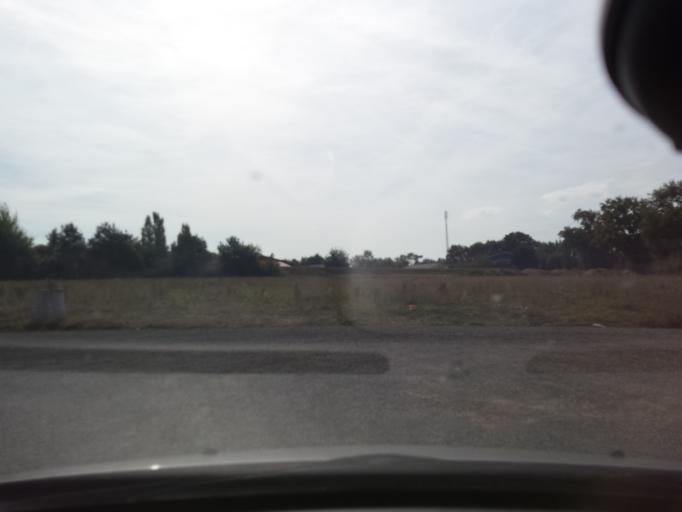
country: FR
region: Pays de la Loire
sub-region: Departement de la Vendee
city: Nieul-le-Dolent
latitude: 46.5721
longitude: -1.5149
